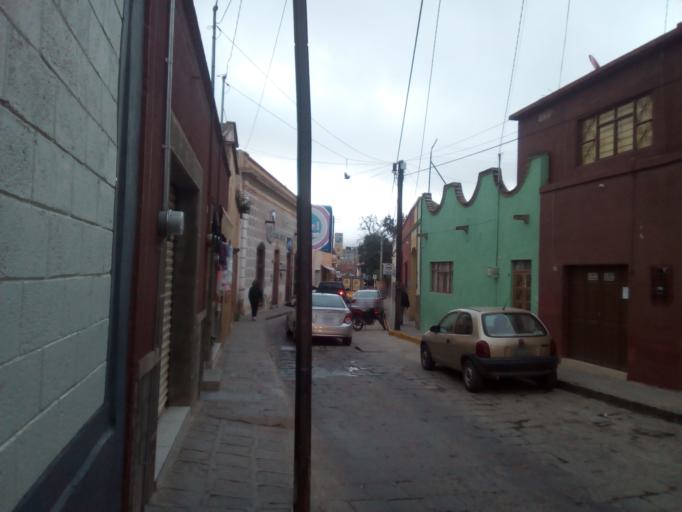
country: MX
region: Guerrero
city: San Luis de la Paz
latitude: 21.2963
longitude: -100.5174
